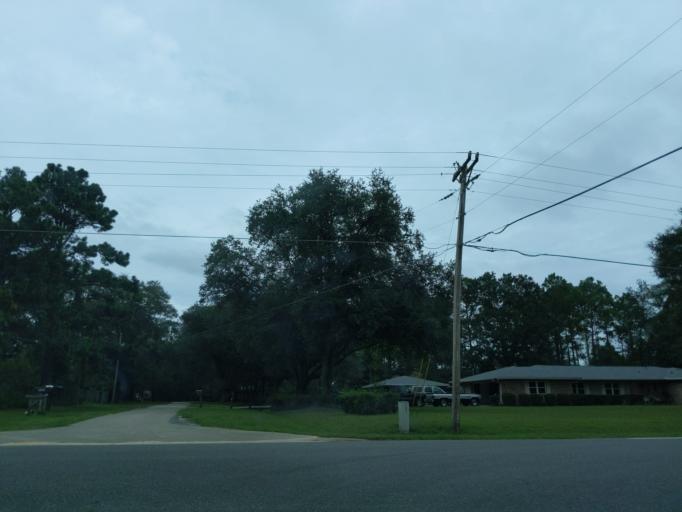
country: US
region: Florida
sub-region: Leon County
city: Woodville
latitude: 30.3793
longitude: -84.1469
